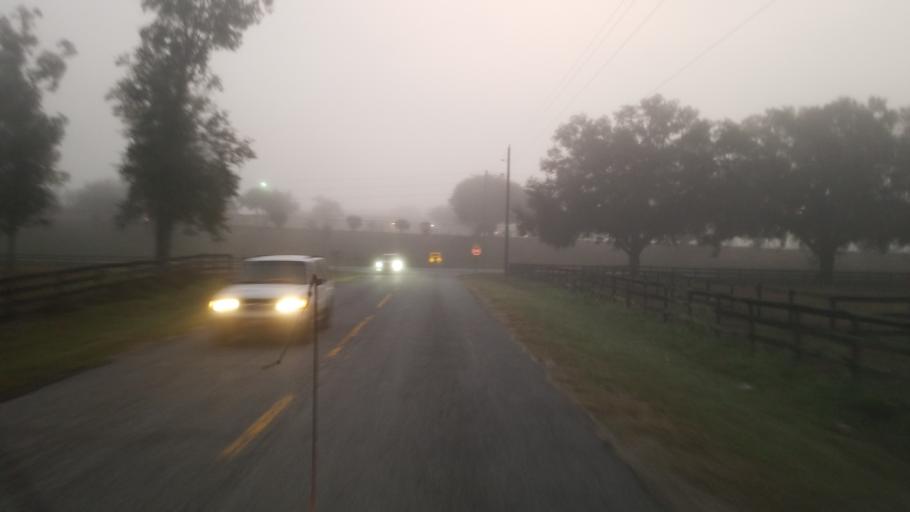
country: US
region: Florida
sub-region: Marion County
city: Ocala
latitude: 29.1539
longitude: -82.2527
